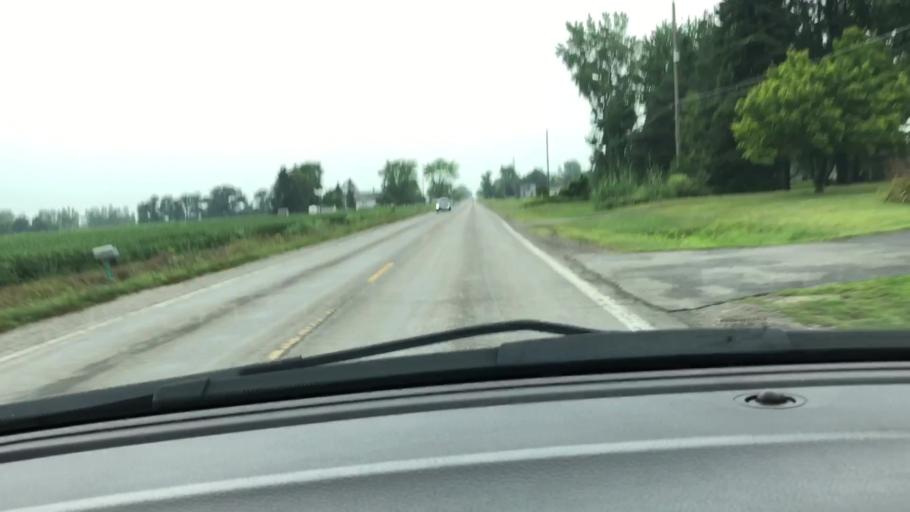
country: US
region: Michigan
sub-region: Saginaw County
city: Freeland
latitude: 43.4982
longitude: -84.0911
